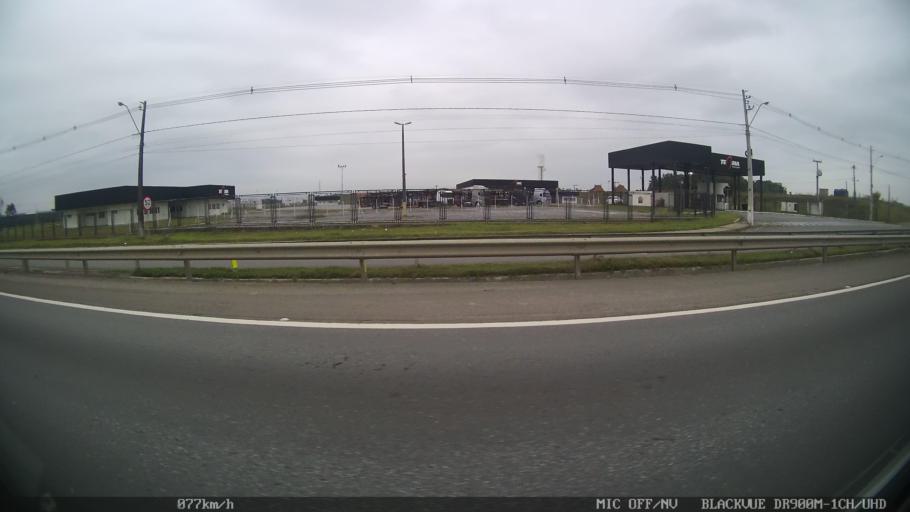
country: BR
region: Santa Catarina
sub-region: Barra Velha
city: Barra Velha
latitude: -26.4654
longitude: -48.7496
